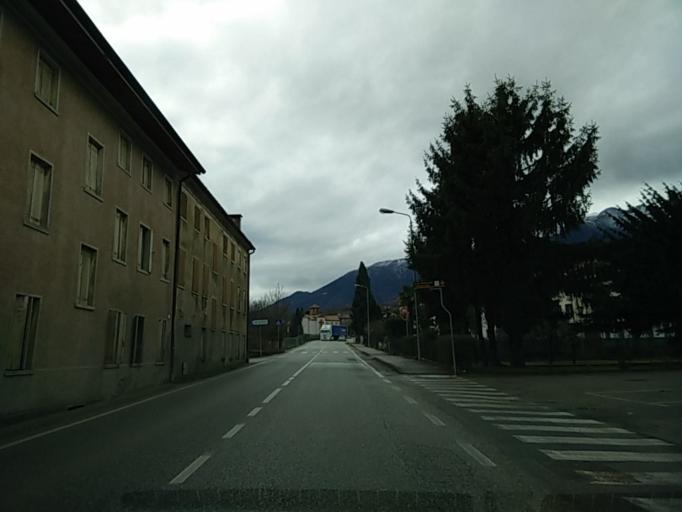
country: IT
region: Veneto
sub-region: Provincia di Treviso
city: Caniezza
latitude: 45.8536
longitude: 11.8929
